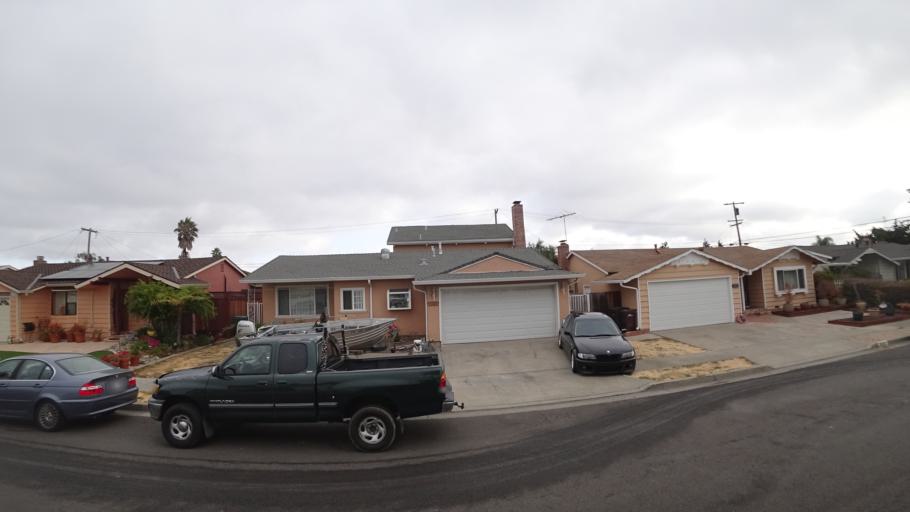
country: US
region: California
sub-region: Alameda County
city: Hayward
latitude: 37.6438
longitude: -122.0972
